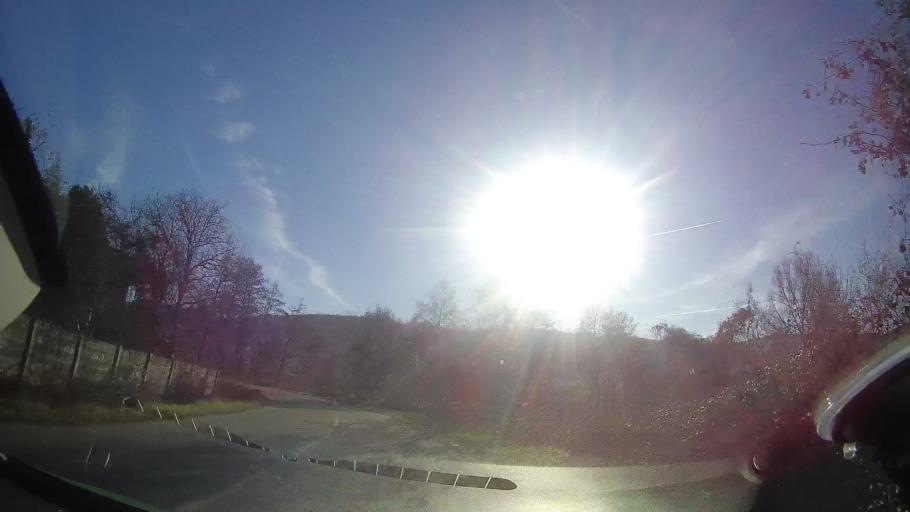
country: RO
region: Bihor
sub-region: Comuna Suncuius
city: Suncuius
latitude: 46.9476
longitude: 22.5375
